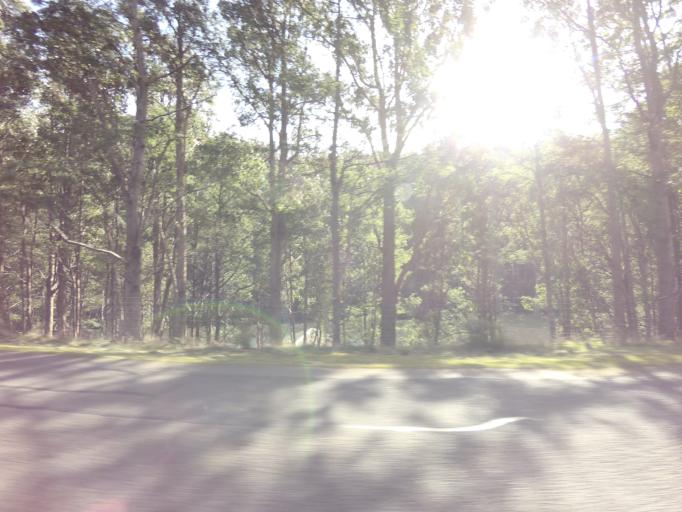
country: AU
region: Tasmania
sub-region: Huon Valley
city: Huonville
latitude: -43.0420
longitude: 147.1264
